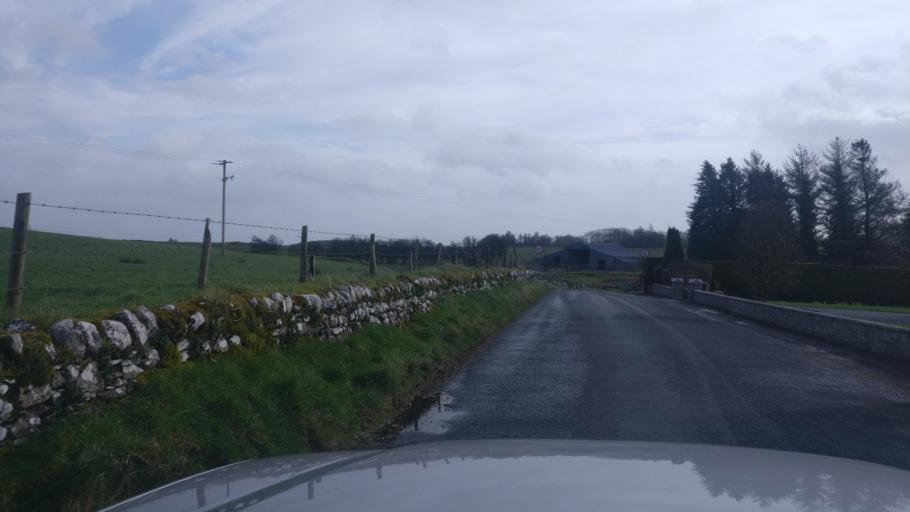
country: IE
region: Connaught
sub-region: County Galway
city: Loughrea
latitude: 53.3018
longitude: -8.4863
